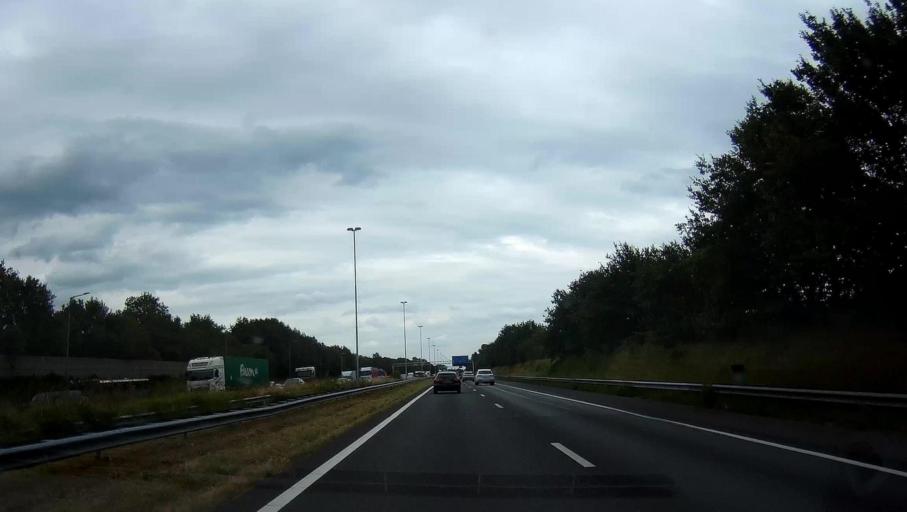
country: NL
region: North Brabant
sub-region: Gemeente Breda
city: Breda
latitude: 51.5456
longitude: 4.8220
